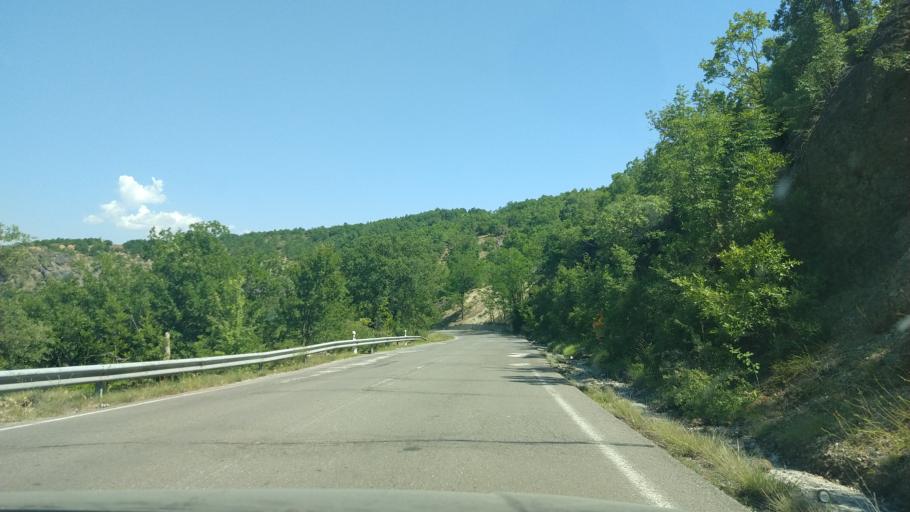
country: GR
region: West Macedonia
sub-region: Nomos Grevenon
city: Grevena
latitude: 40.0500
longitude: 21.4824
